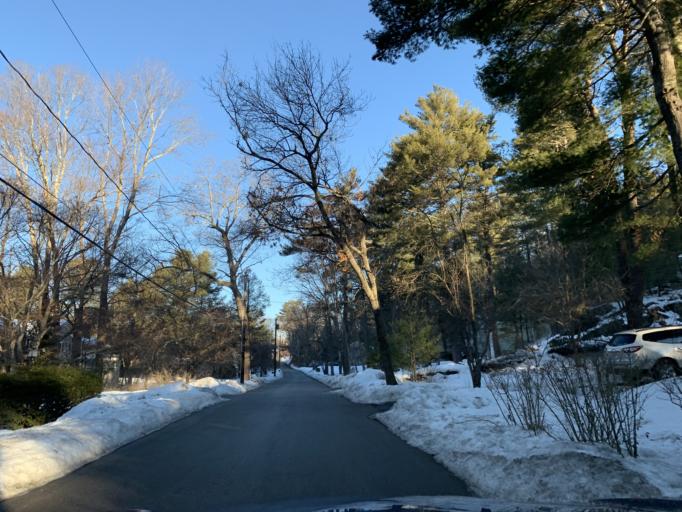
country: US
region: Massachusetts
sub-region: Norfolk County
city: Westwood
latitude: 42.2103
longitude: -71.2384
